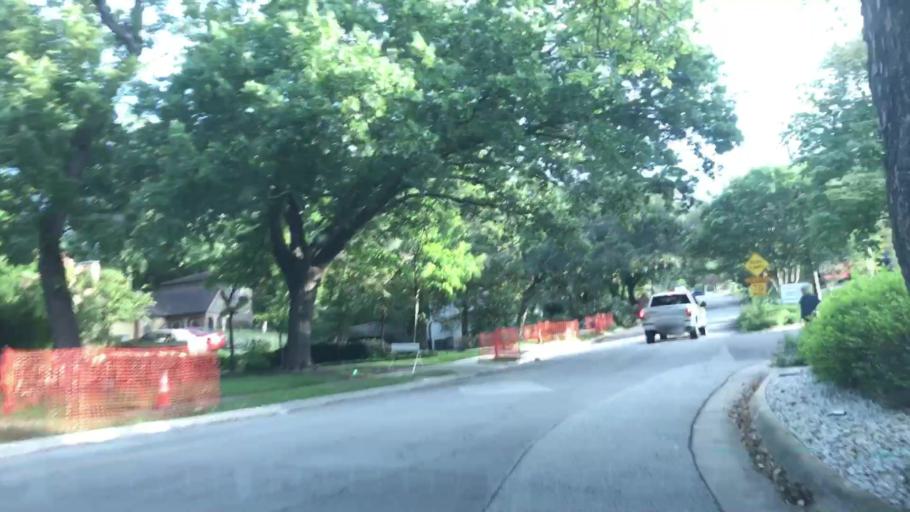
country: US
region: Texas
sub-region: Dallas County
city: Cockrell Hill
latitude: 32.7584
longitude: -96.8467
